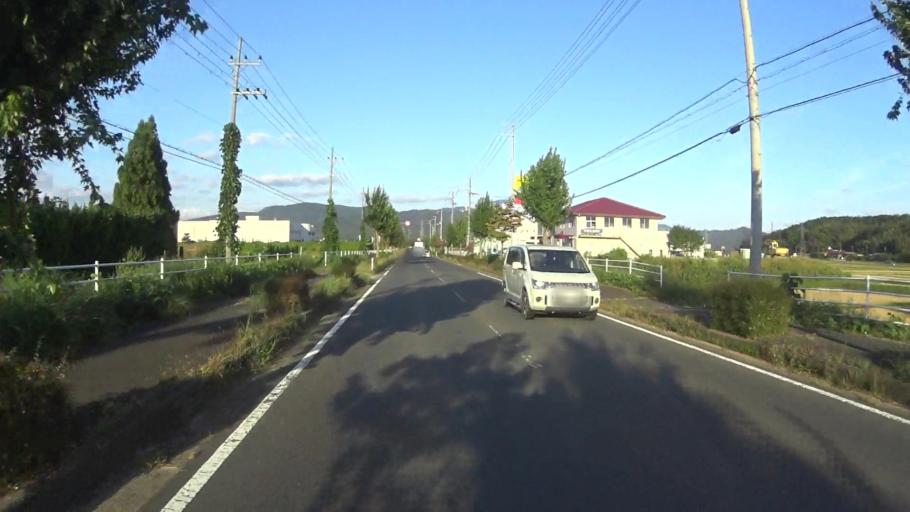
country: JP
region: Kyoto
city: Miyazu
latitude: 35.6078
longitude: 135.0598
